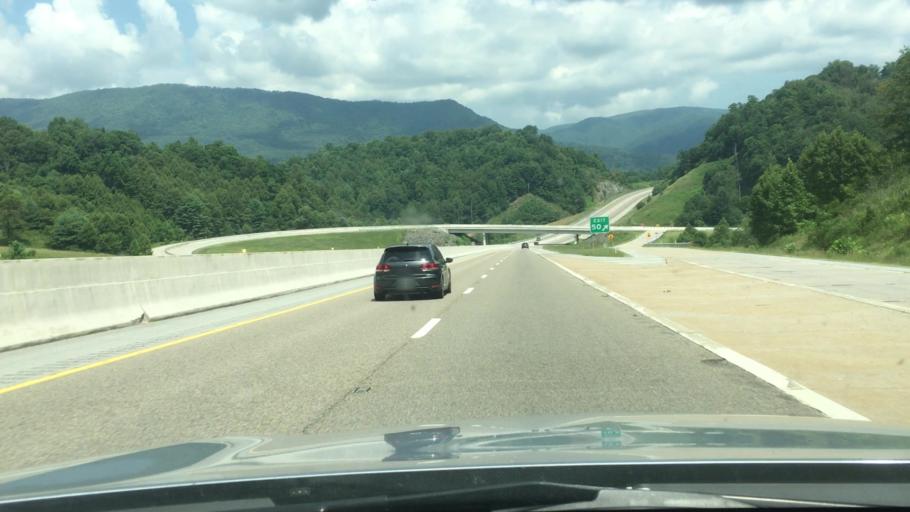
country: US
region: Tennessee
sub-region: Unicoi County
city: Banner Hill
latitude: 36.0090
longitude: -82.5446
